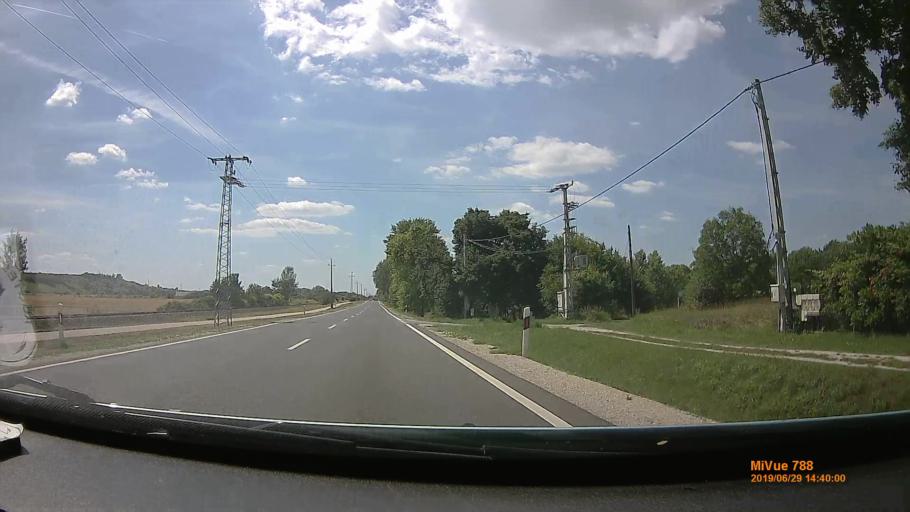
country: HU
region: Komarom-Esztergom
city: Nyergesujfalu
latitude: 47.7550
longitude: 18.5945
